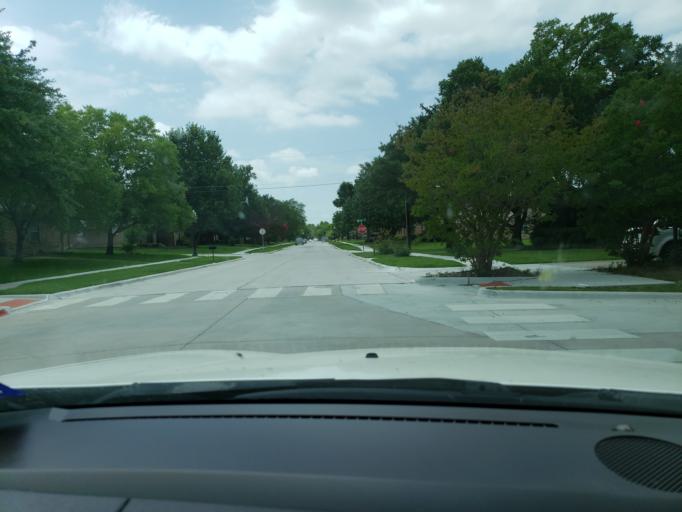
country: US
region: Texas
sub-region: Dallas County
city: Rowlett
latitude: 32.9007
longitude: -96.5641
